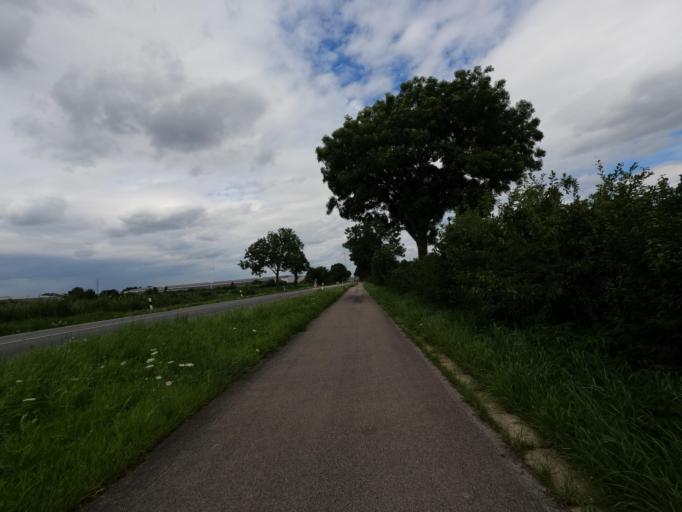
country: DE
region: North Rhine-Westphalia
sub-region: Regierungsbezirk Koln
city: Ubach-Palenberg
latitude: 50.9231
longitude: 6.1367
